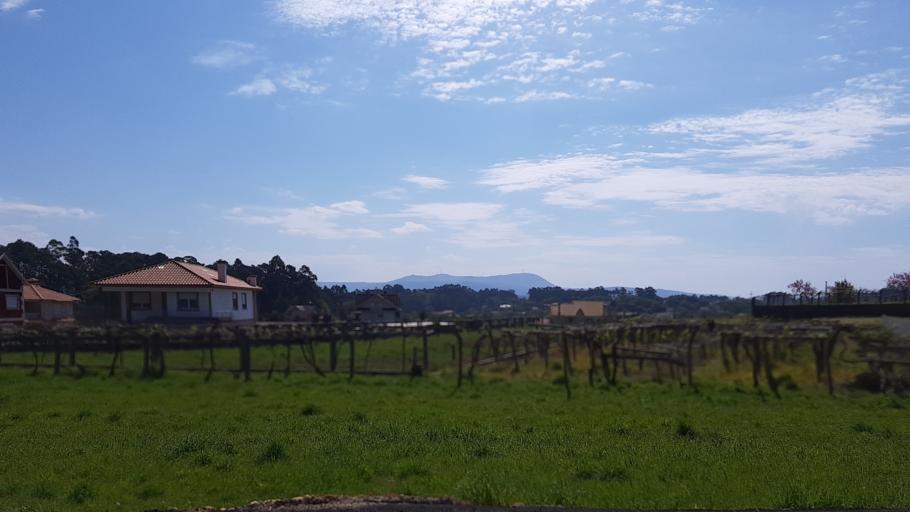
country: ES
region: Galicia
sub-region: Provincia de Pontevedra
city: O Rosal
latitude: 41.9387
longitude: -8.8526
